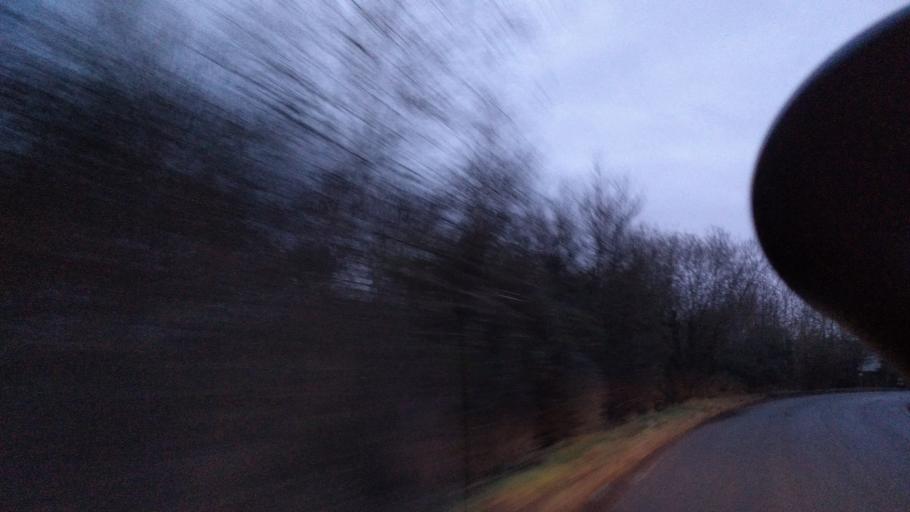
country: GB
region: England
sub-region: Borough of Swindon
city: Highworth
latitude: 51.5841
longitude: -1.7281
